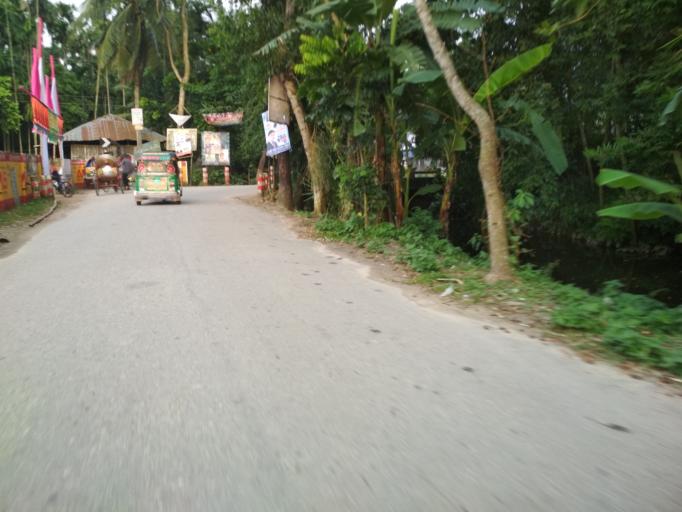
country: BD
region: Chittagong
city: Raipur
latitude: 23.0064
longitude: 90.7071
